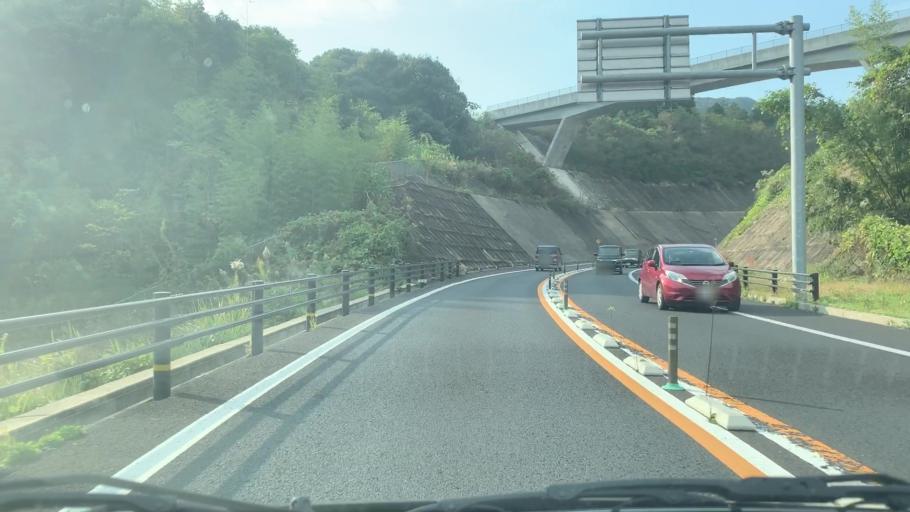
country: JP
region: Nagasaki
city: Sasebo
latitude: 32.9962
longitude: 129.7309
